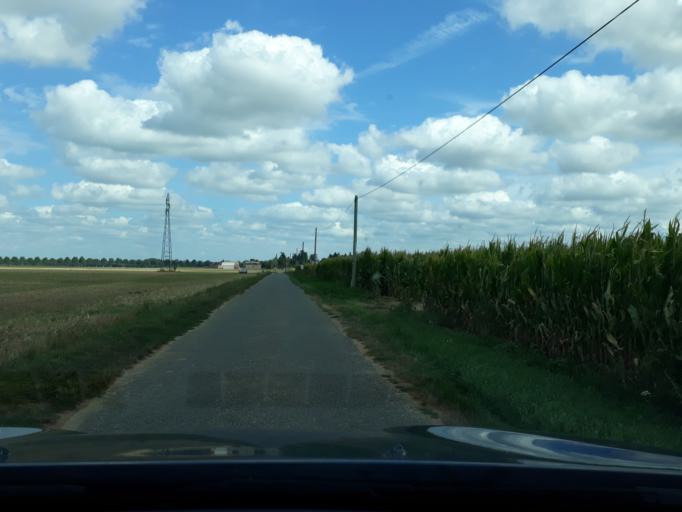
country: FR
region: Centre
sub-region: Departement du Loiret
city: Saint-Cyr-en-Val
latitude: 47.8386
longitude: 1.9789
